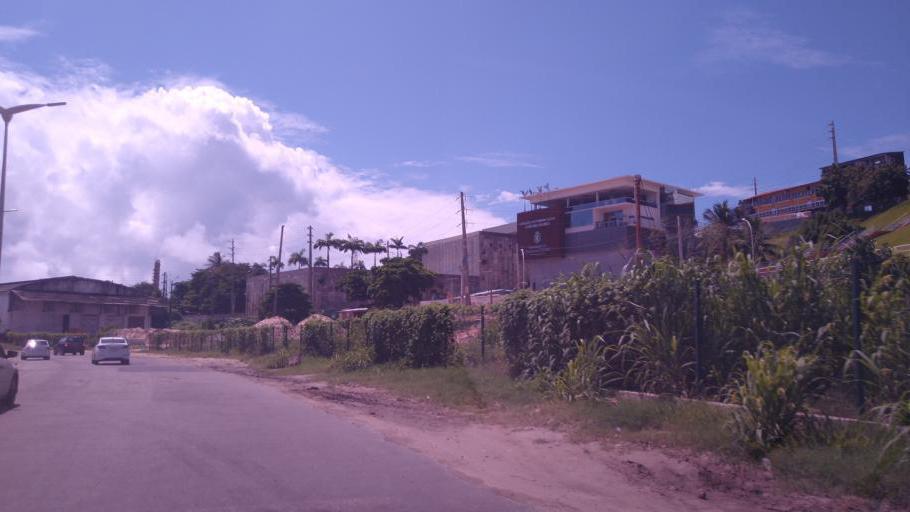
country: BR
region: Ceara
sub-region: Fortaleza
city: Fortaleza
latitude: -3.7197
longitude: -38.4757
